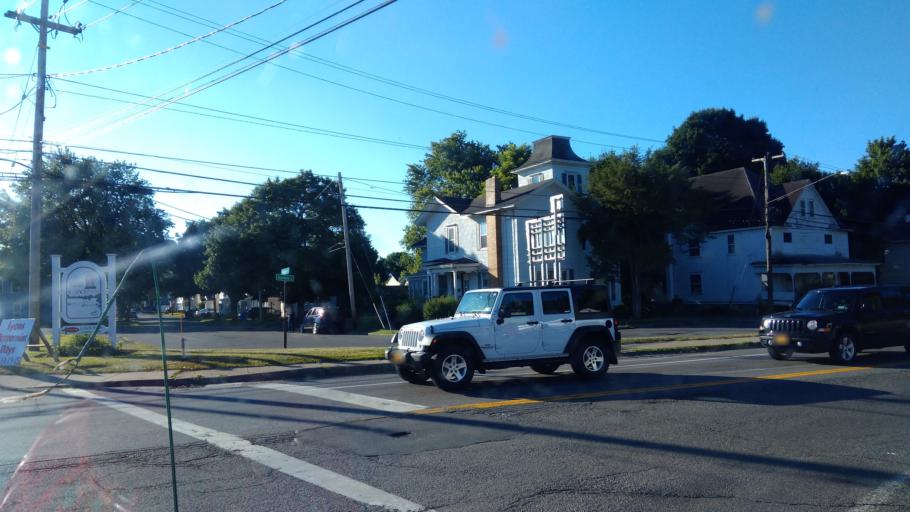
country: US
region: New York
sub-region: Wayne County
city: Lyons
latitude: 43.0596
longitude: -76.9925
